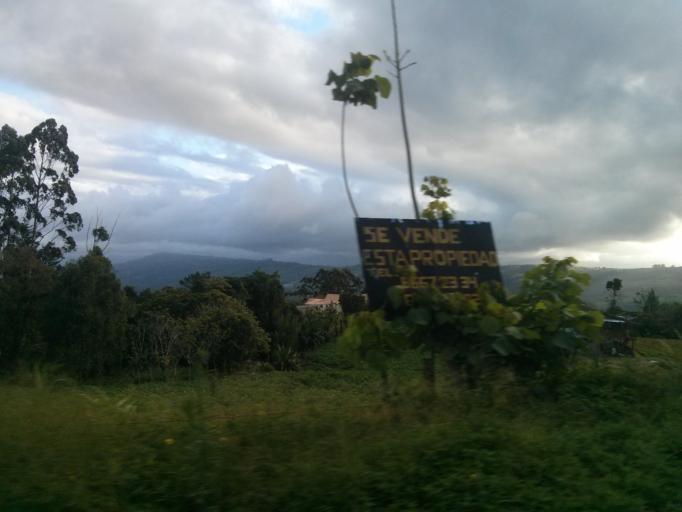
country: CR
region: Cartago
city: Turrialba
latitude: 9.9587
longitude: -83.7188
